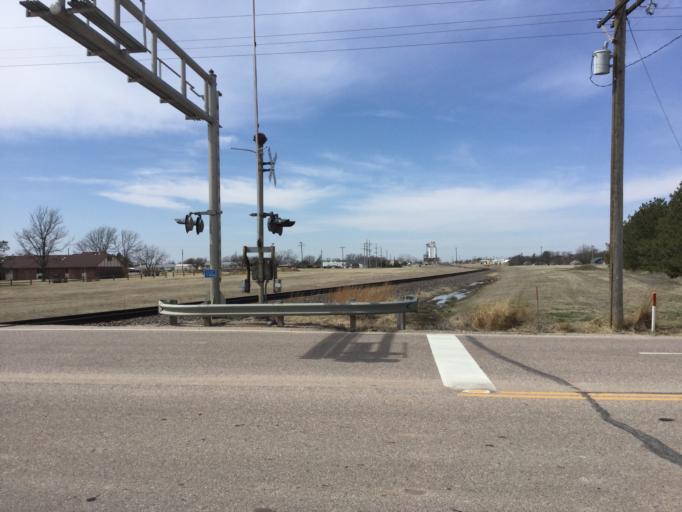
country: US
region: Kansas
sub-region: Trego County
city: WaKeeney
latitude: 39.0230
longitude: -99.8715
